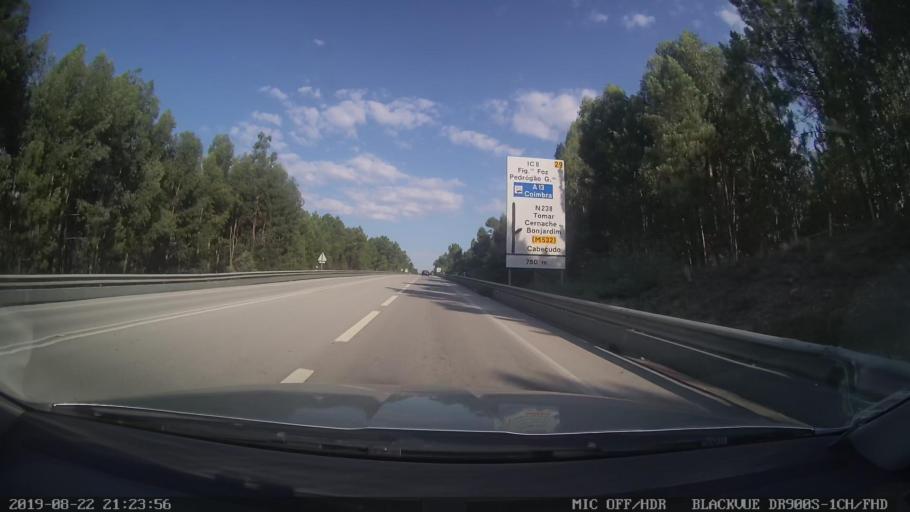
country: PT
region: Castelo Branco
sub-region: Serta
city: Serta
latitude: 39.8366
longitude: -8.1147
